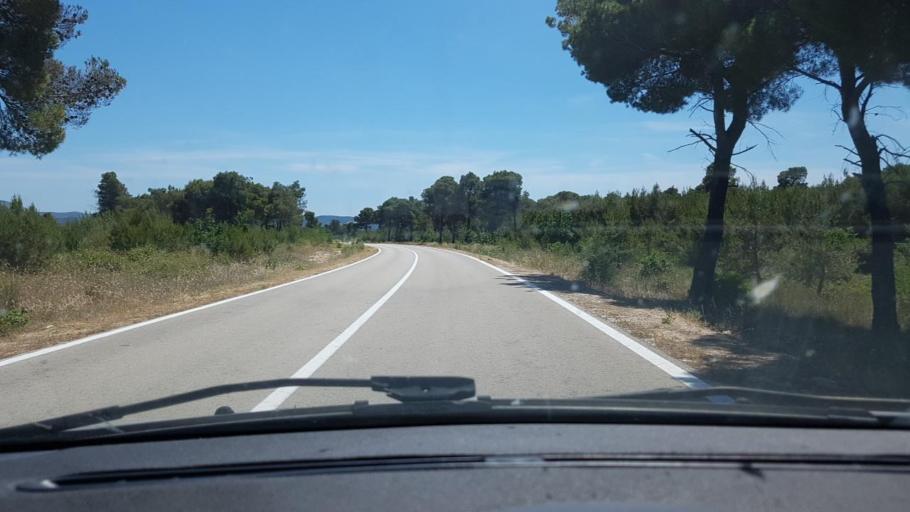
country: HR
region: Sibensko-Kniniska
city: Zaton
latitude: 43.8563
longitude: 15.9100
